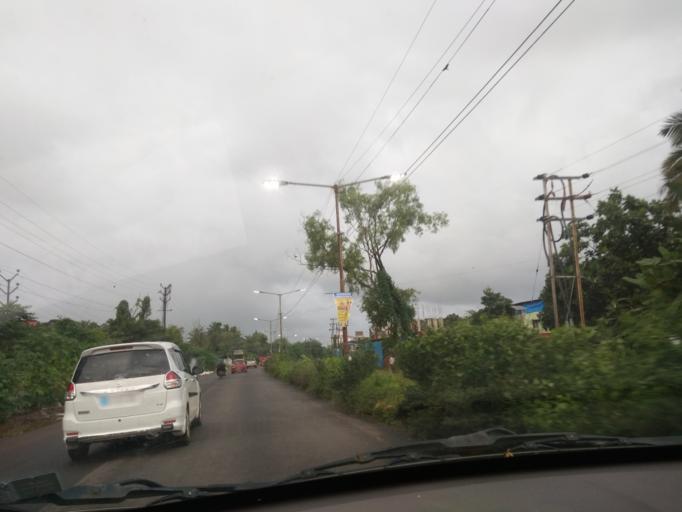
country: IN
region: Goa
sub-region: South Goa
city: Davorlim
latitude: 15.2762
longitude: 73.9807
